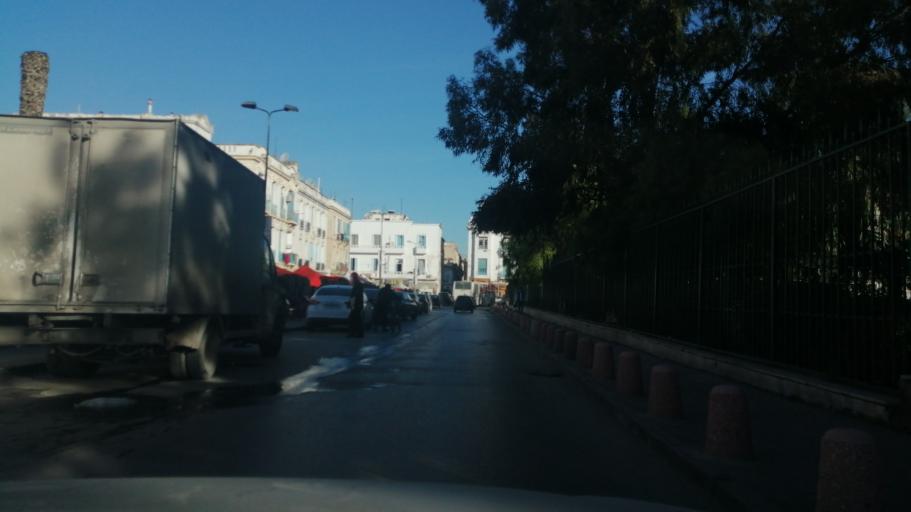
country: TN
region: Tunis
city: Tunis
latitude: 36.8047
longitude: 10.1765
